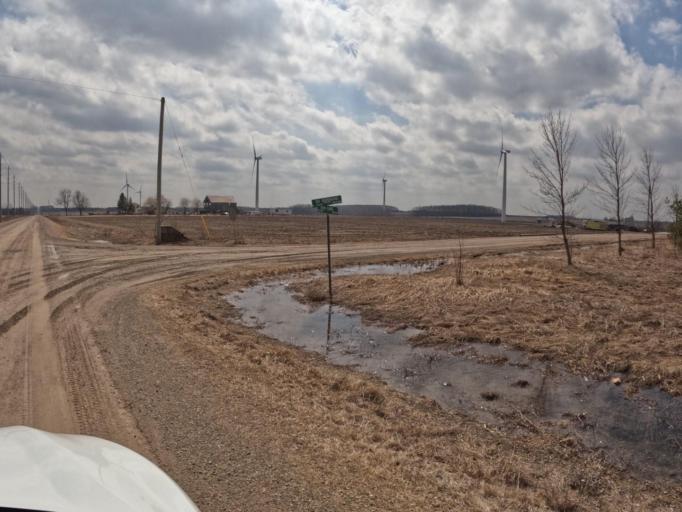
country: CA
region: Ontario
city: Shelburne
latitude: 44.0450
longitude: -80.3186
